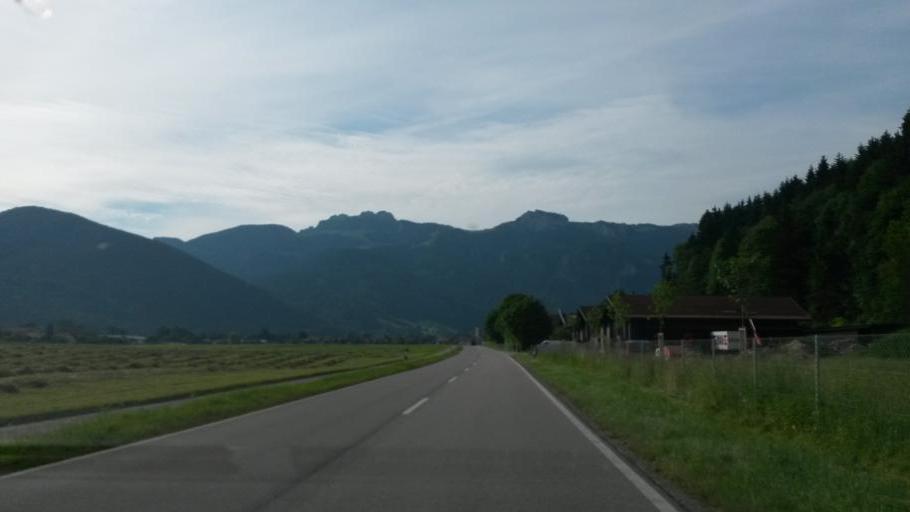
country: DE
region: Bavaria
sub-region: Upper Bavaria
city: Aschau im Chiemgau
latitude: 47.7904
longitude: 12.3105
